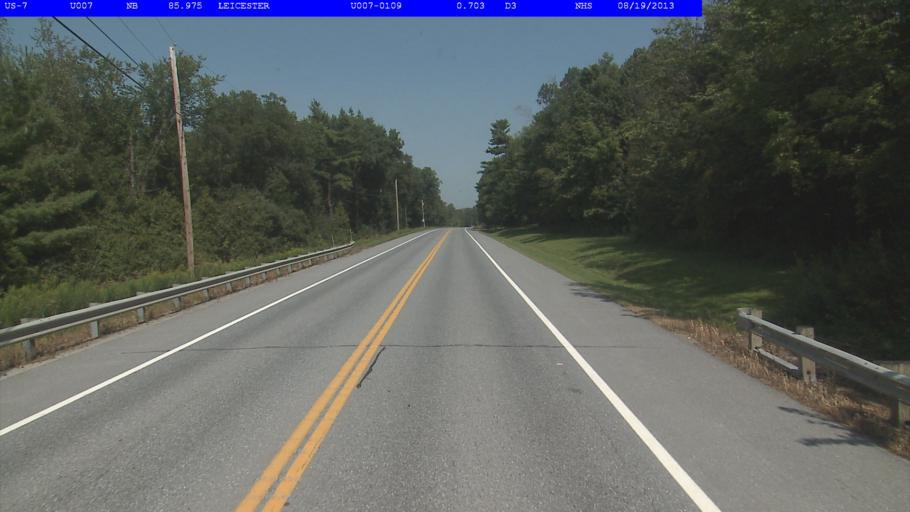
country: US
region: Vermont
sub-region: Rutland County
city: Brandon
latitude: 43.8534
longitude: -73.1063
